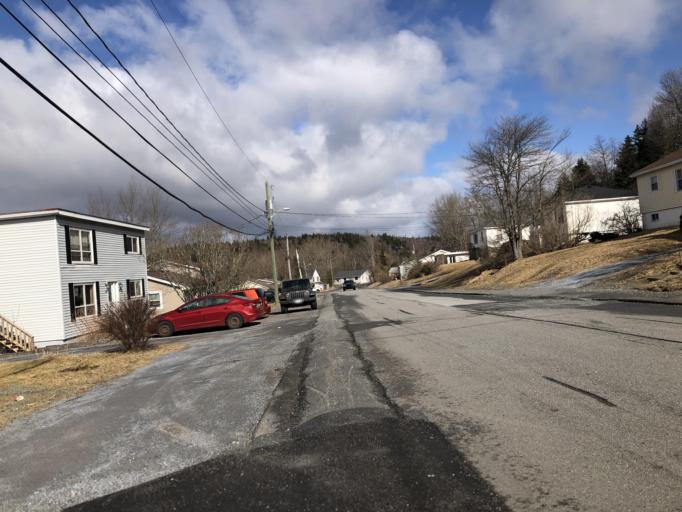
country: CA
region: New Brunswick
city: Saint John
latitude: 45.3205
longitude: -66.0101
